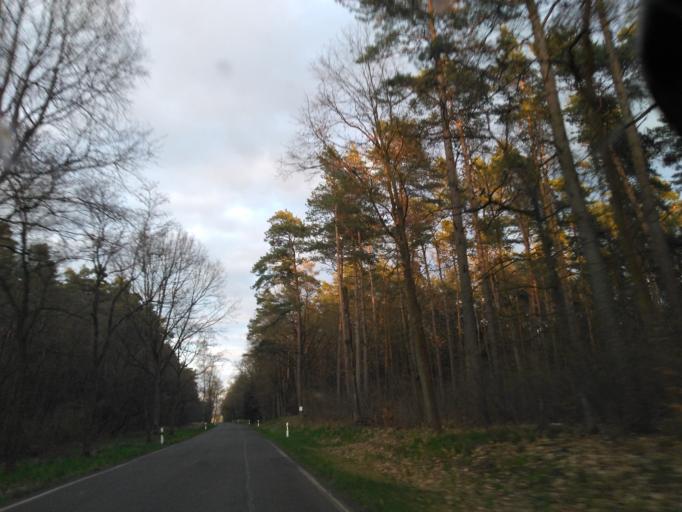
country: DE
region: Brandenburg
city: Buckow
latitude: 52.6113
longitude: 14.0474
